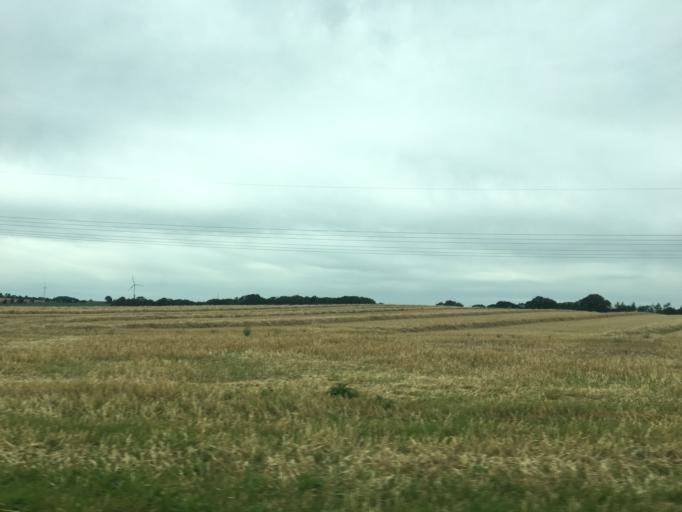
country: DE
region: Saxony
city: Wilsdruff
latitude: 51.0693
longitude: 13.5958
